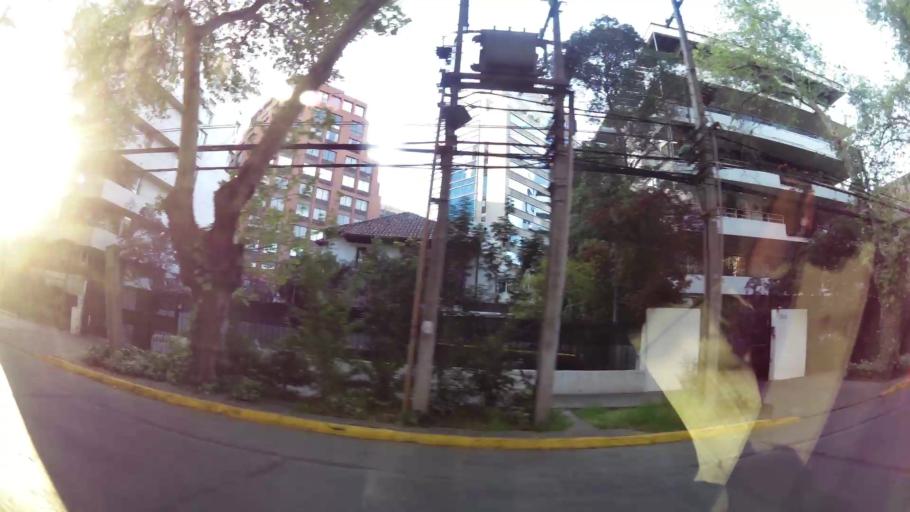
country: CL
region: Santiago Metropolitan
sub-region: Provincia de Santiago
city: Villa Presidente Frei, Nunoa, Santiago, Chile
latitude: -33.4239
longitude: -70.6077
